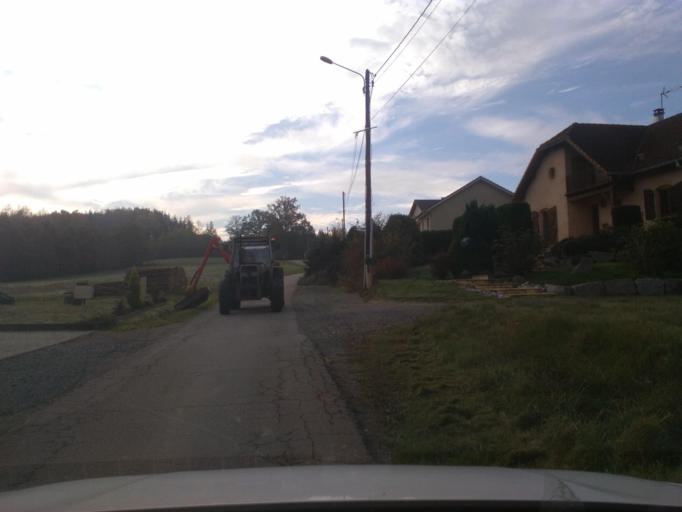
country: FR
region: Lorraine
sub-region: Departement des Vosges
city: Saint-Michel-sur-Meurthe
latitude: 48.3460
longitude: 6.8979
